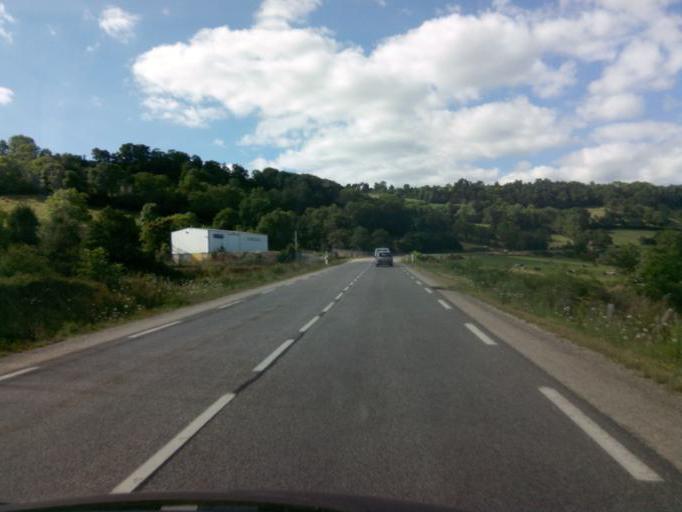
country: FR
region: Auvergne
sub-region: Departement de la Haute-Loire
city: Saint-Paulien
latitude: 45.1439
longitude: 3.8144
